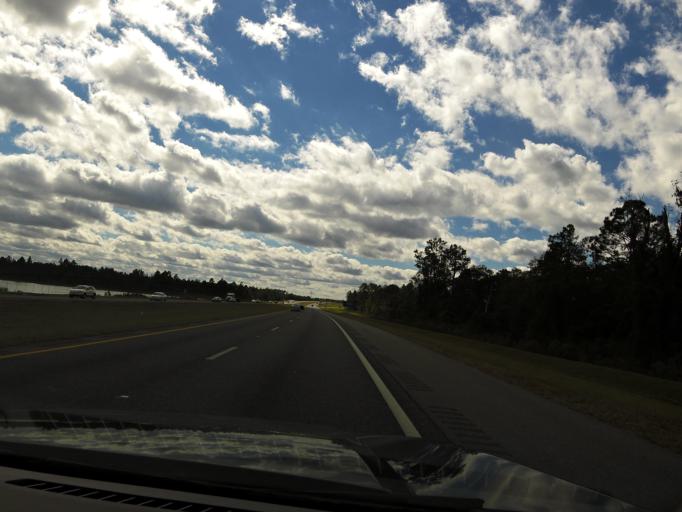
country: US
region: Florida
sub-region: Bradford County
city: Starke
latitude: 29.9810
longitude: -82.1160
